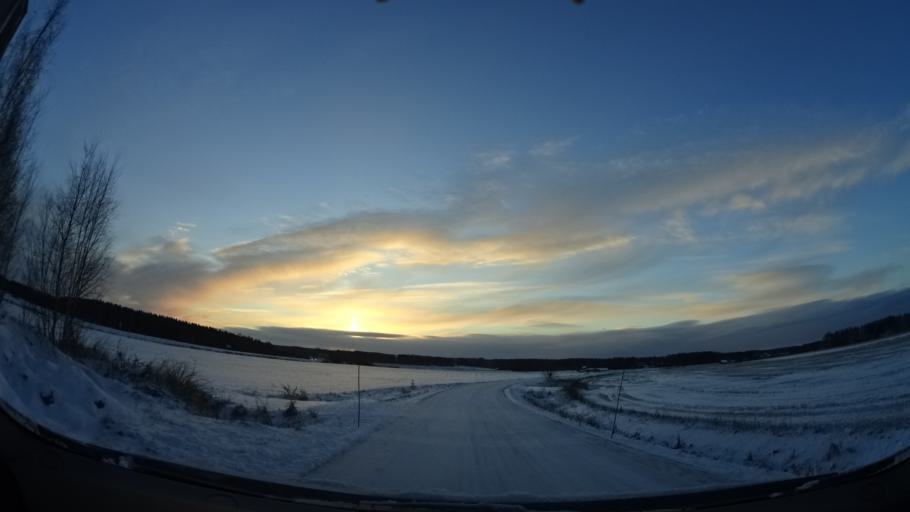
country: SE
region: Vaesterbotten
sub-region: Skelleftea Kommun
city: Kage
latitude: 64.8514
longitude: 20.9914
